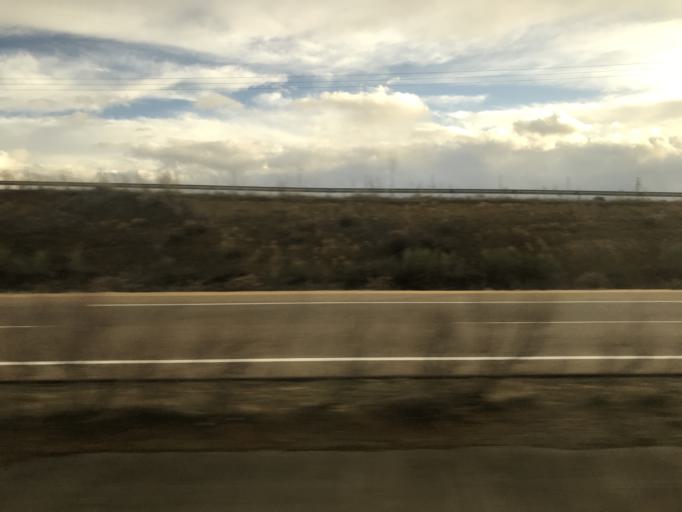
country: ES
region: Castille and Leon
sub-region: Provincia de Palencia
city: Palencia
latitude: 42.0388
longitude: -4.5386
